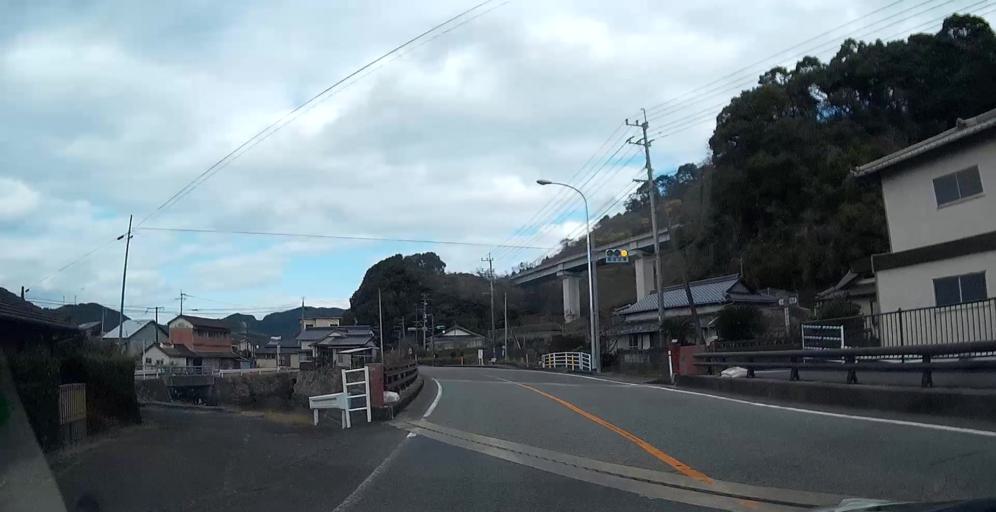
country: JP
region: Kumamoto
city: Minamata
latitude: 32.3535
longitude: 130.5076
